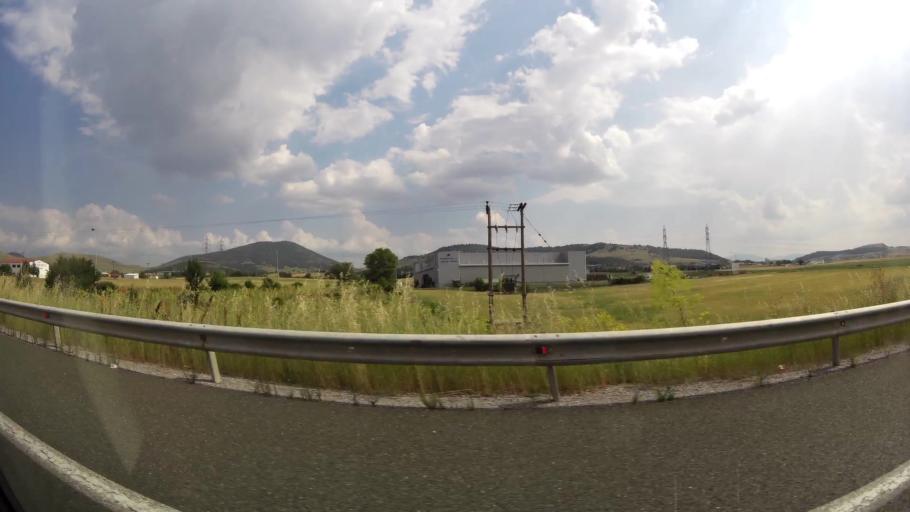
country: GR
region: West Macedonia
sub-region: Nomos Kozanis
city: Koila
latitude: 40.3610
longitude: 21.8426
